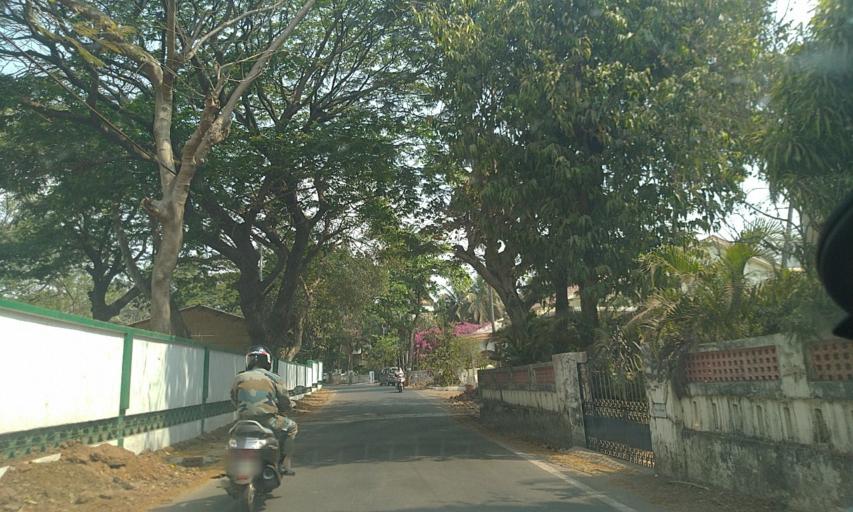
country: IN
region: Goa
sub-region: North Goa
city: Panaji
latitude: 15.4899
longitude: 73.8272
